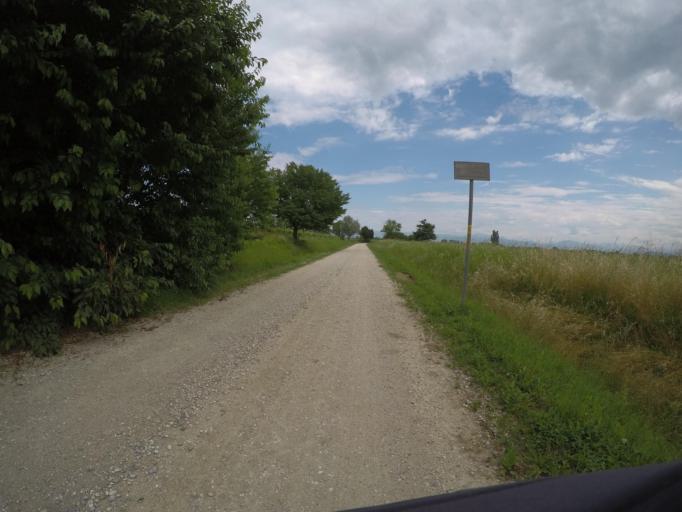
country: IT
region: Friuli Venezia Giulia
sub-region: Provincia di Udine
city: Trivignano Udinese
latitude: 45.9331
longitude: 13.3297
